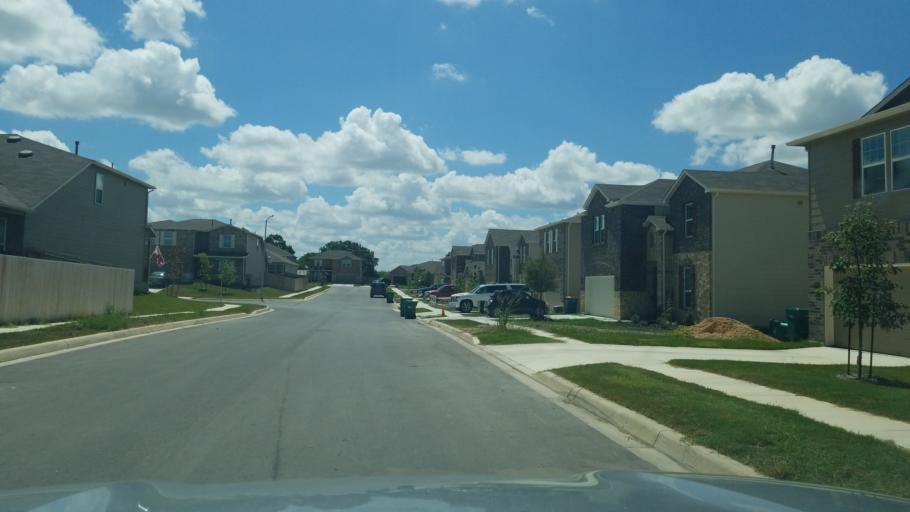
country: US
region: Texas
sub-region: Bexar County
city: Converse
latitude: 29.5352
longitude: -98.3168
